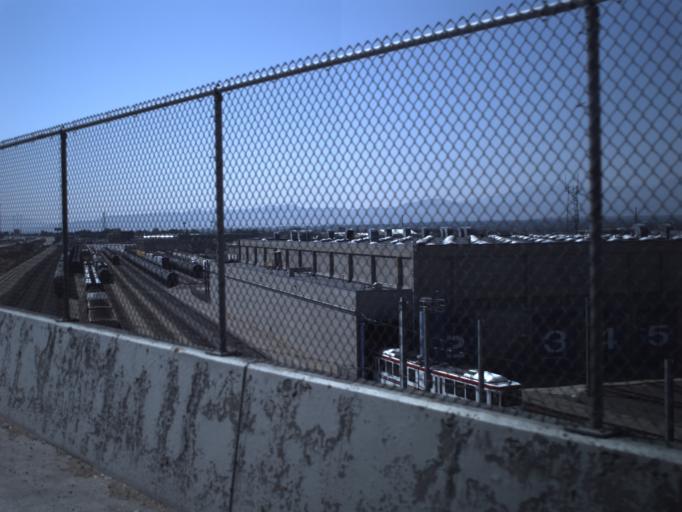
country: US
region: Utah
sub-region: Salt Lake County
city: Midvale
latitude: 40.6285
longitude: -111.9038
